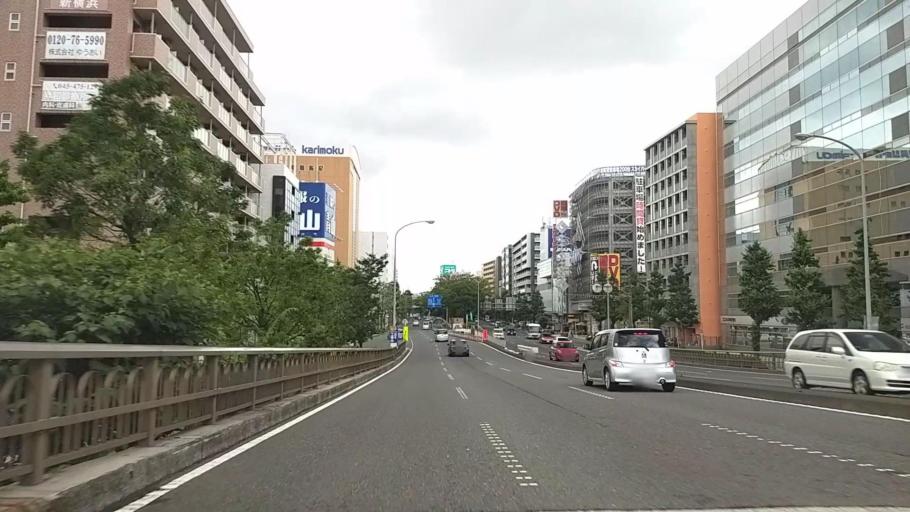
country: JP
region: Kanagawa
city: Yokohama
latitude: 35.5054
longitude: 139.6128
